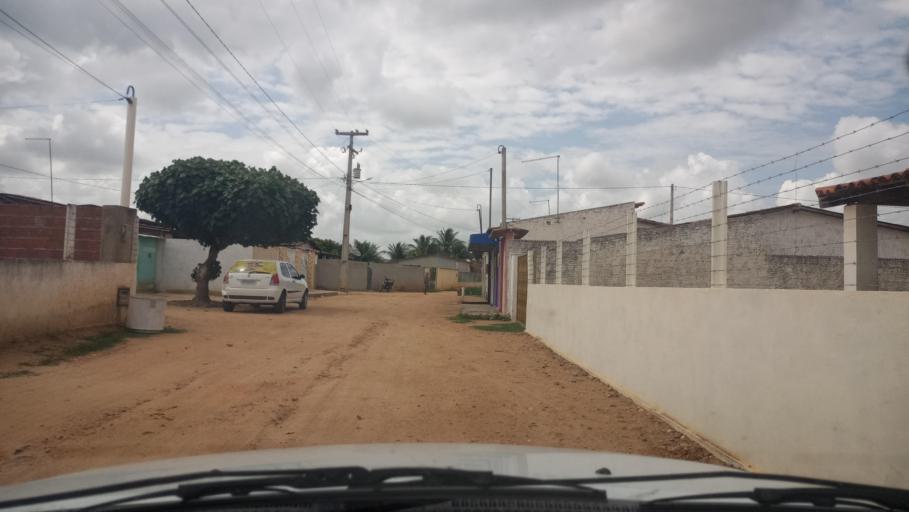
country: BR
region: Rio Grande do Norte
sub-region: Sao Paulo Do Potengi
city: Sao Paulo do Potengi
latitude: -5.9113
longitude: -35.6953
